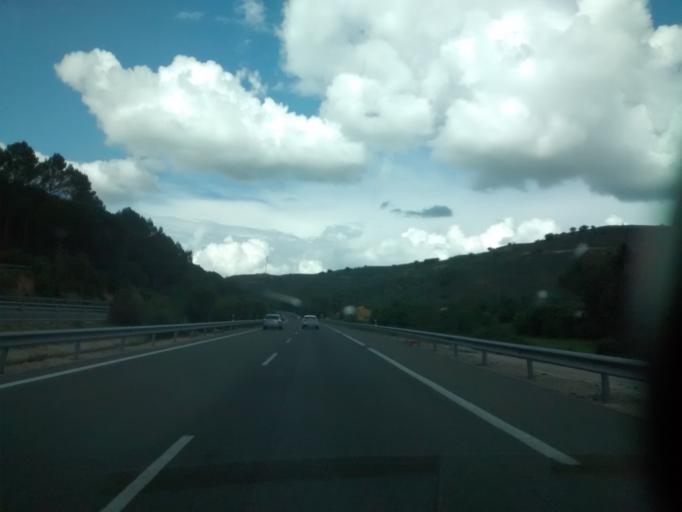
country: ES
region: Castille-La Mancha
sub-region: Provincia de Guadalajara
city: Torija
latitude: 40.7269
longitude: -3.0514
